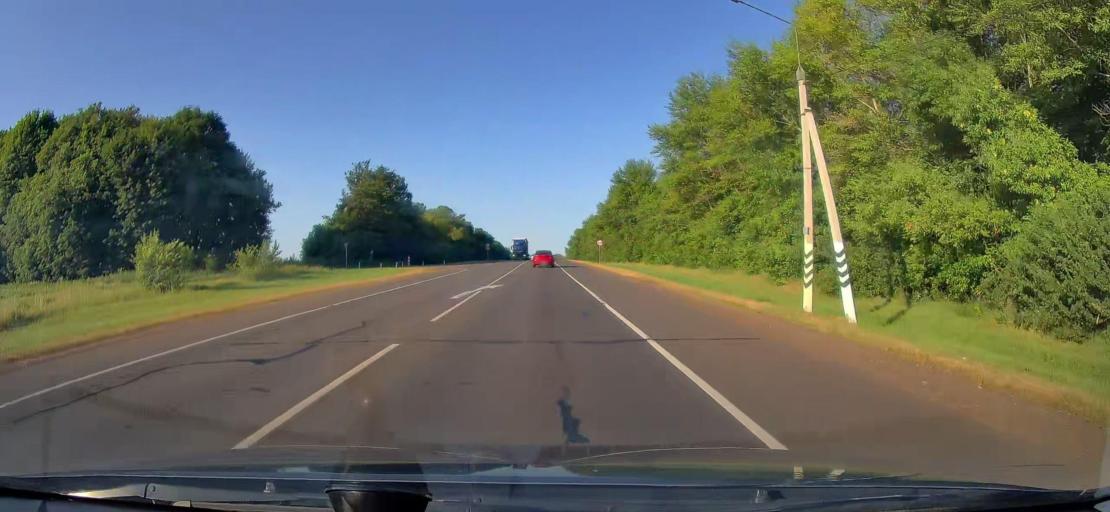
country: RU
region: Tula
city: Plavsk
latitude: 53.6200
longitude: 37.1903
